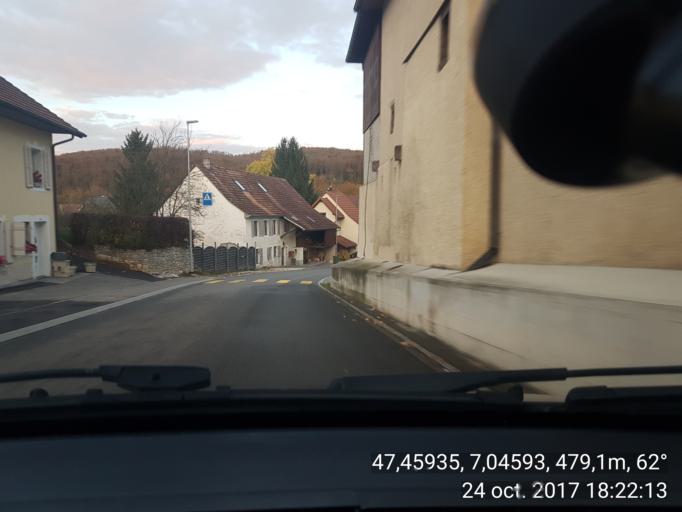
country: CH
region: Jura
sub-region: Porrentruy District
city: Boncourt
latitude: 47.4592
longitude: 7.0456
